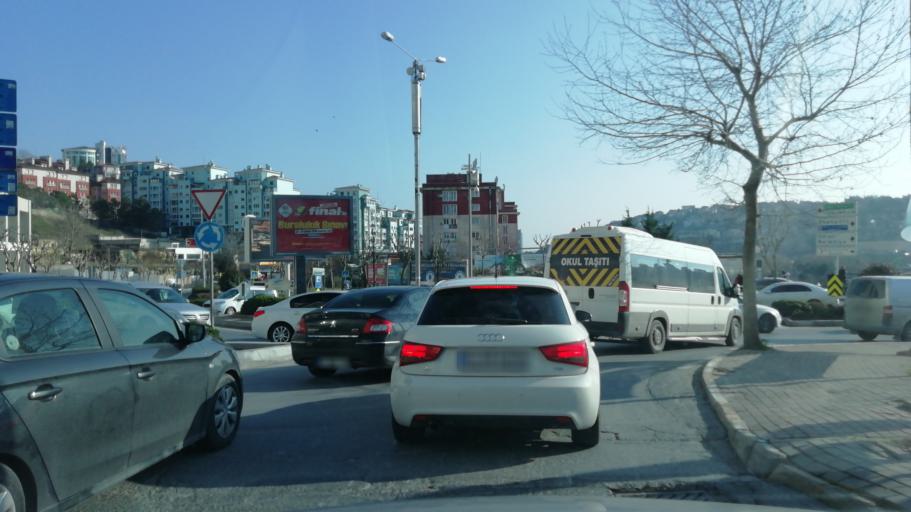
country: TR
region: Istanbul
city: Esenyurt
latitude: 41.0734
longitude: 28.6924
